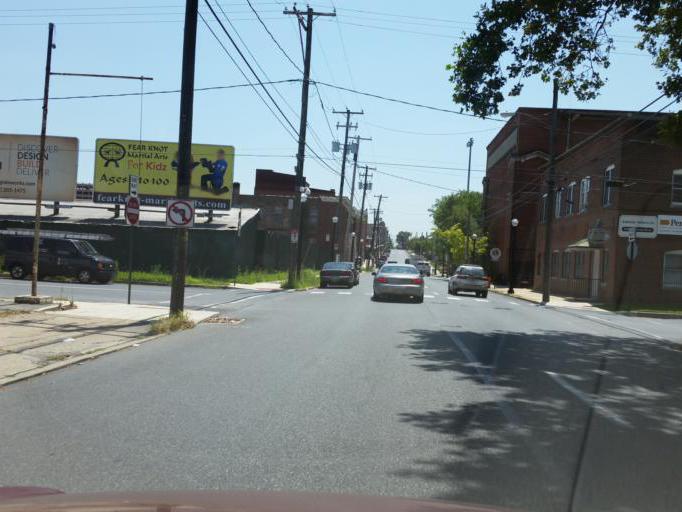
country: US
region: Pennsylvania
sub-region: Lancaster County
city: Lancaster
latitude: 40.0510
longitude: -76.3101
